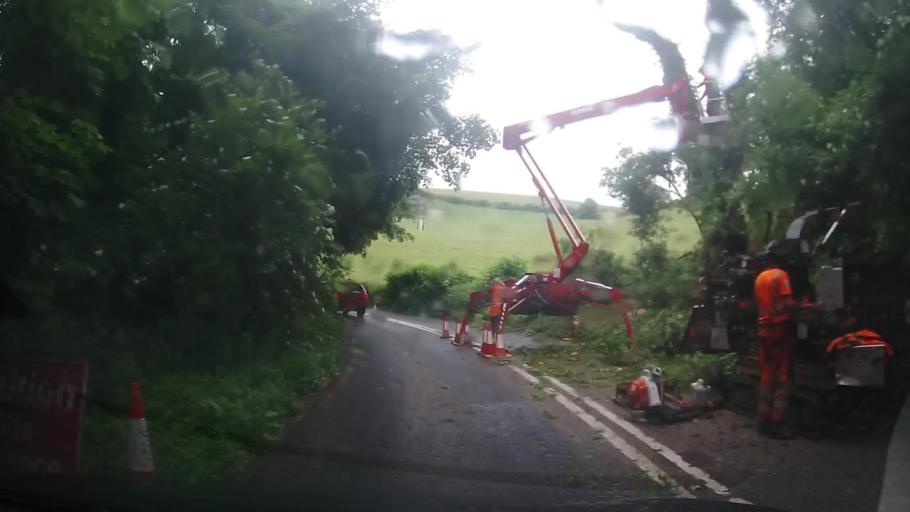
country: GB
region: England
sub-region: Devon
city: Dartmouth
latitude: 50.3639
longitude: -3.5724
